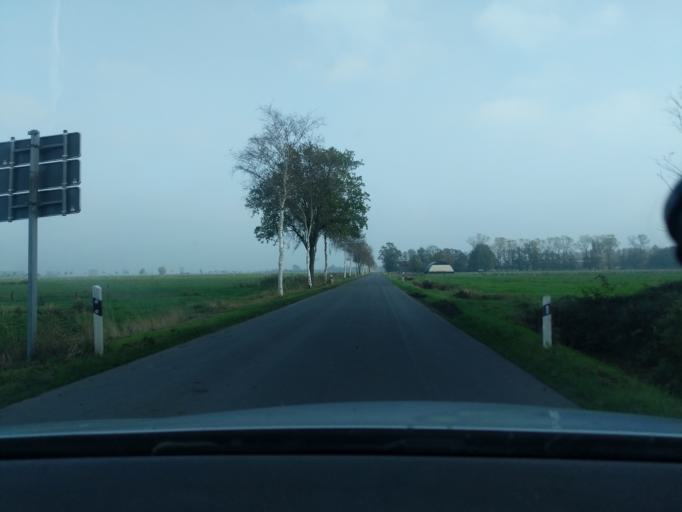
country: DE
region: Lower Saxony
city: Wanna
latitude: 53.7256
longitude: 8.7952
